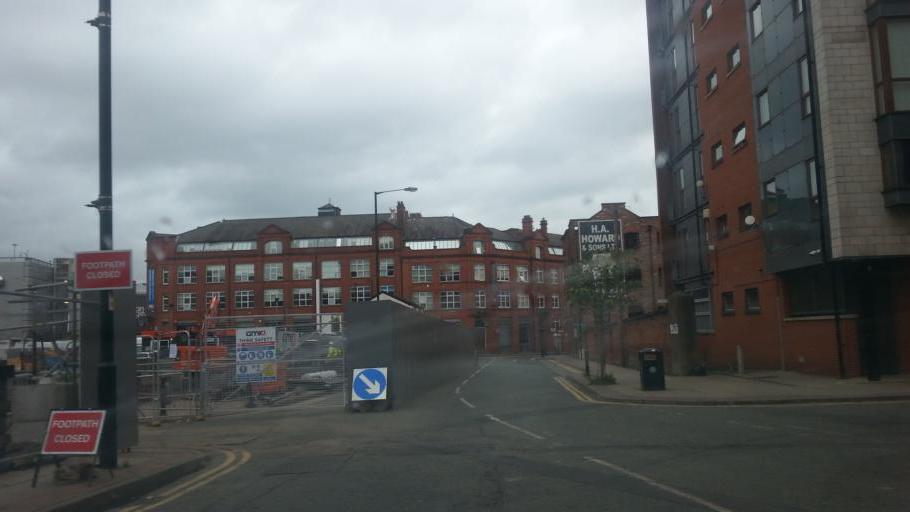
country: GB
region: England
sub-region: Manchester
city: Manchester
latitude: 53.4798
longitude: -2.2300
